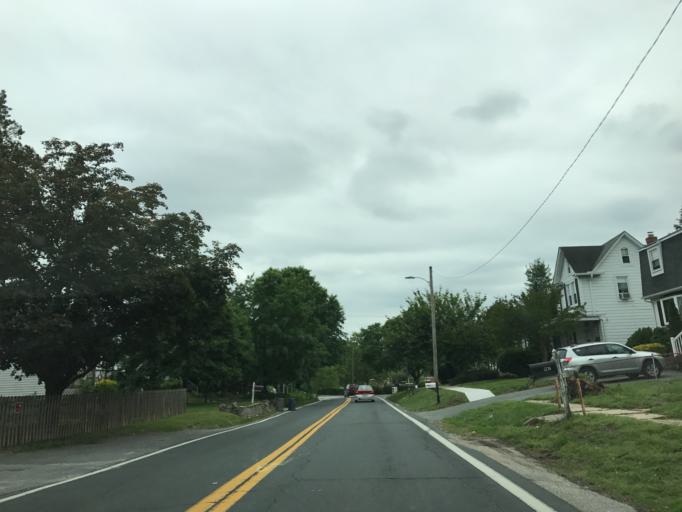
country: US
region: Maryland
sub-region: Baltimore County
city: Arbutus
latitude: 39.2509
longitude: -76.6885
